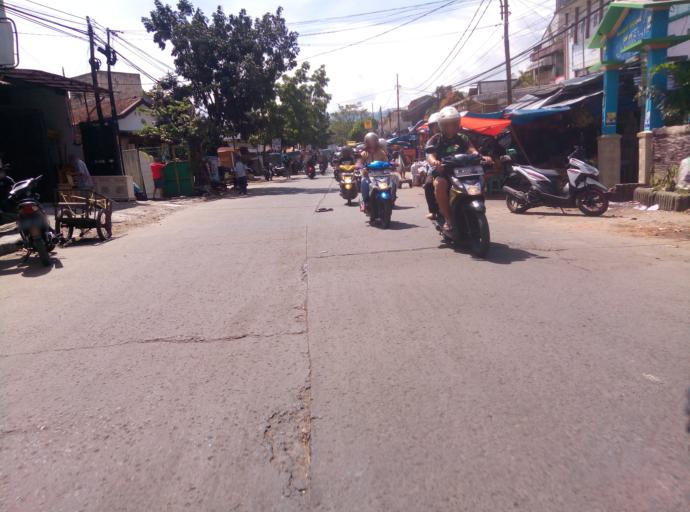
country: ID
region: West Java
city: Bandung
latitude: -6.9054
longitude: 107.6438
